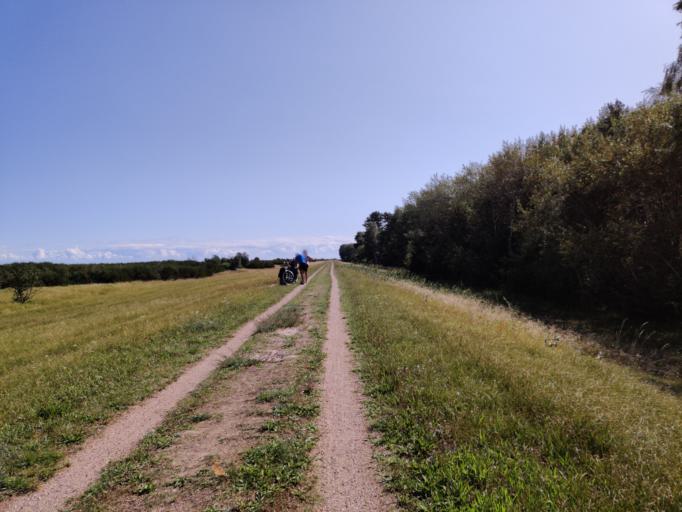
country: DK
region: Zealand
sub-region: Guldborgsund Kommune
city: Nykobing Falster
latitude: 54.6102
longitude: 11.9655
